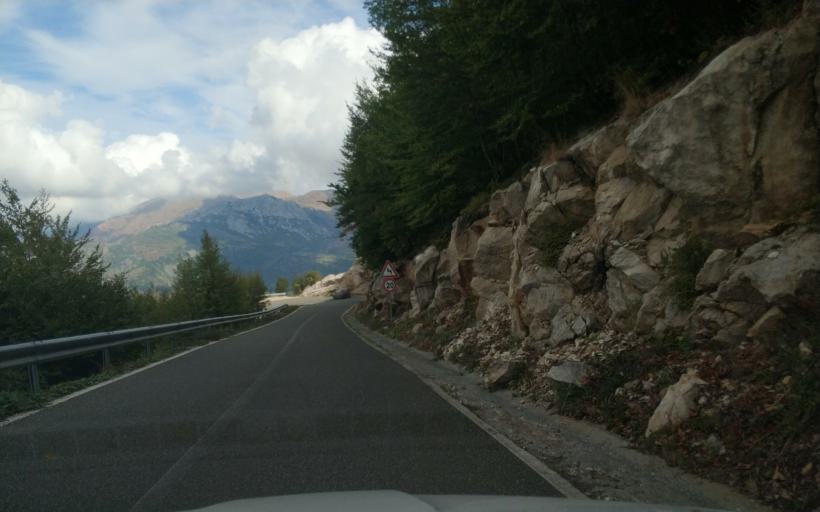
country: AL
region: Durres
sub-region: Rrethi i Krujes
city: Kruje
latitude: 41.5234
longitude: 19.8079
